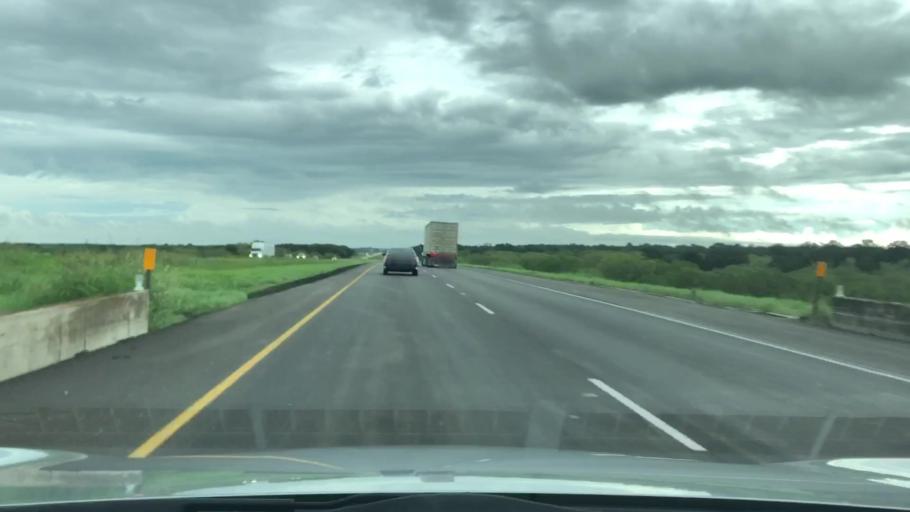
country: US
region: Texas
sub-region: Gonzales County
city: Gonzales
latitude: 29.6496
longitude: -97.4838
